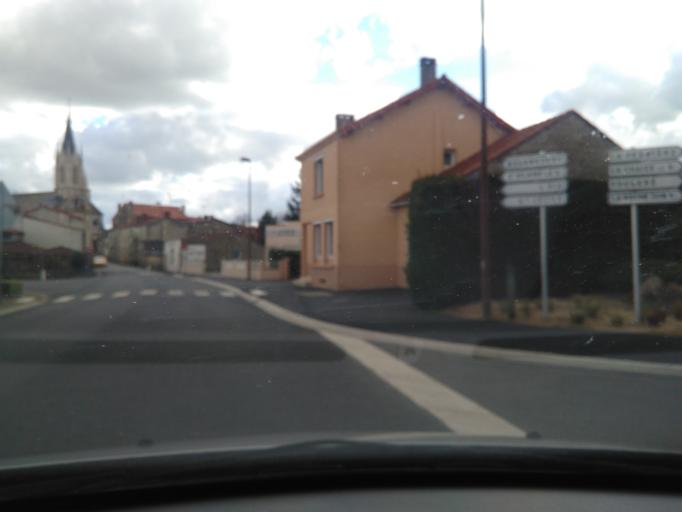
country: FR
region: Pays de la Loire
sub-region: Departement de la Vendee
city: Saint-Martin-des-Noyers
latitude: 46.7229
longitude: -1.1797
